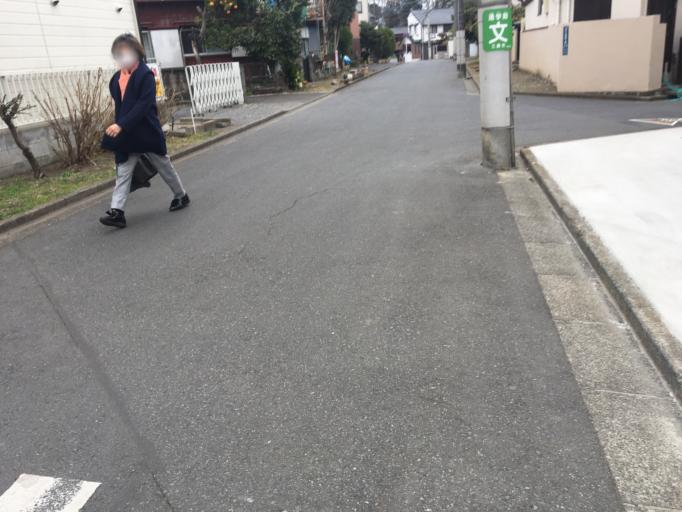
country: JP
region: Tokyo
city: Musashino
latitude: 35.6979
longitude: 139.5761
